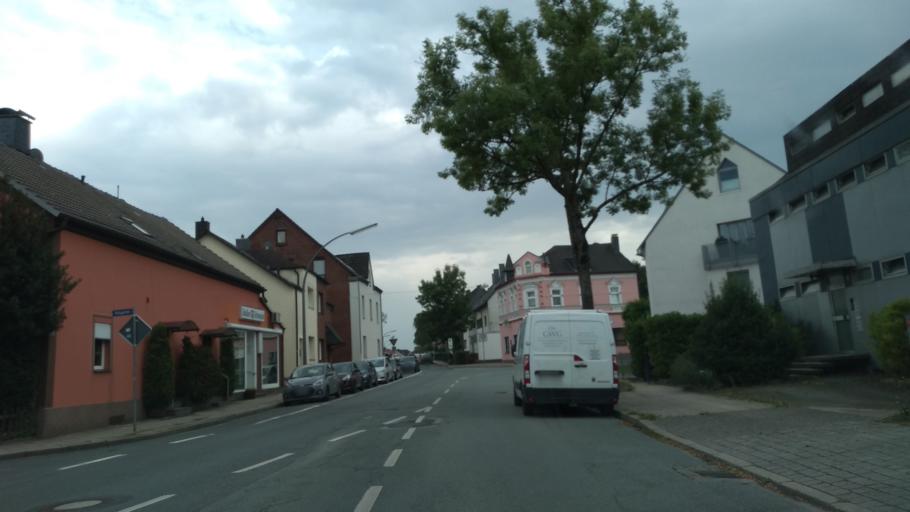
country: DE
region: North Rhine-Westphalia
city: Hattingen
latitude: 51.4432
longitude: 7.1600
